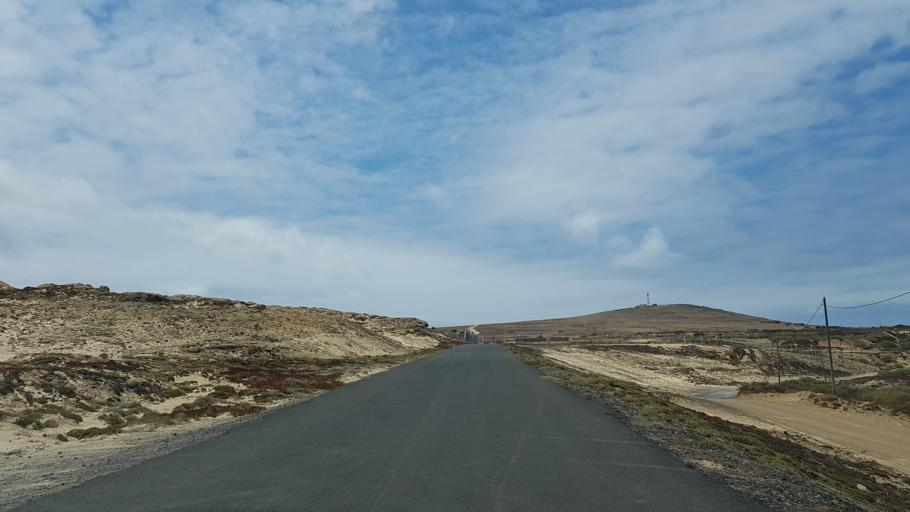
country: PT
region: Madeira
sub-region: Porto Santo
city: Camacha
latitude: 33.0831
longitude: -16.3584
